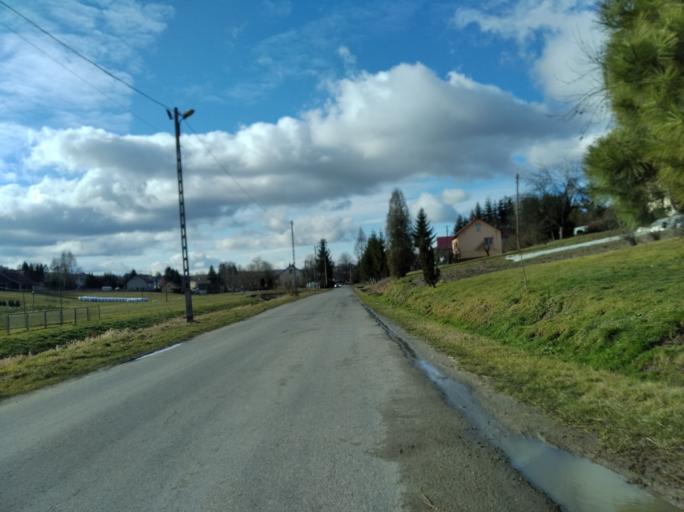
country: PL
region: Subcarpathian Voivodeship
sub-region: Powiat strzyzowski
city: Wisniowa
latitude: 49.9145
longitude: 21.7153
